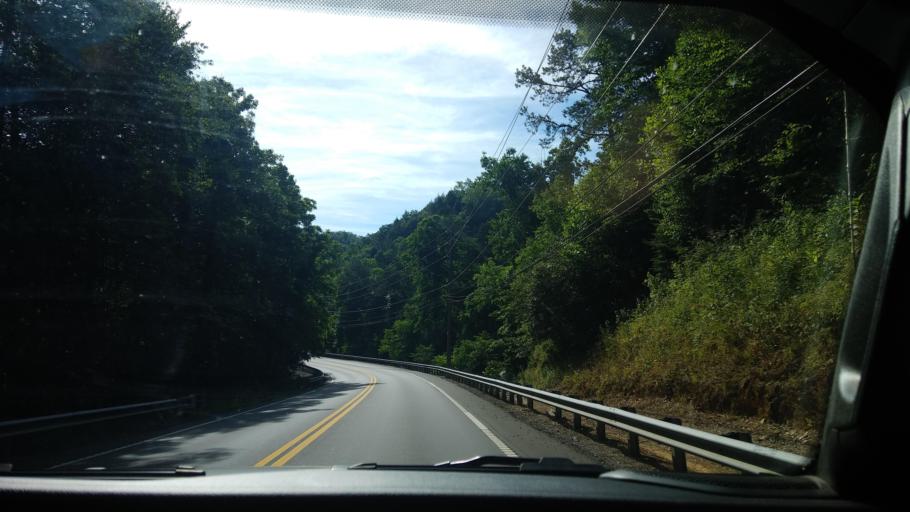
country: US
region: Tennessee
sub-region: Sevier County
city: Gatlinburg
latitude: 35.7497
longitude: -83.3970
